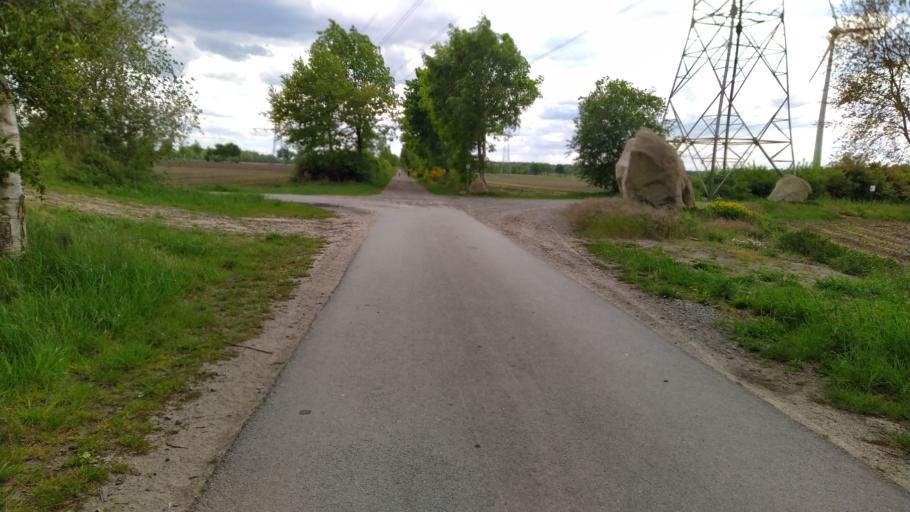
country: DE
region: Lower Saxony
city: Ahlerstedt
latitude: 53.3801
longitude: 9.3986
